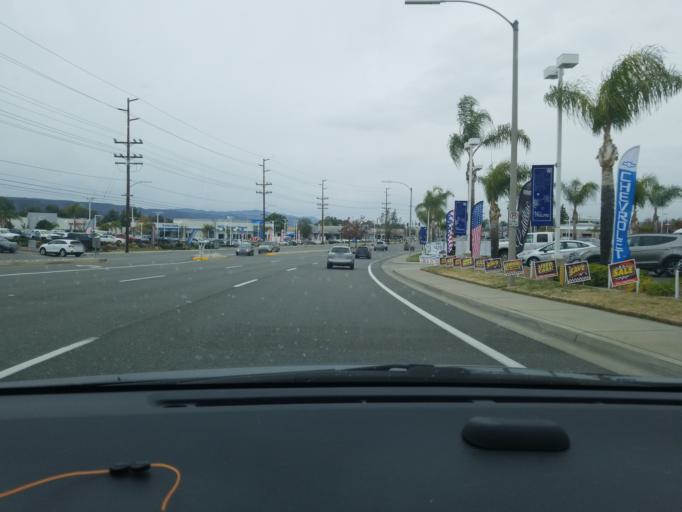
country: US
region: California
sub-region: Riverside County
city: Temecula
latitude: 33.5131
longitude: -117.1537
